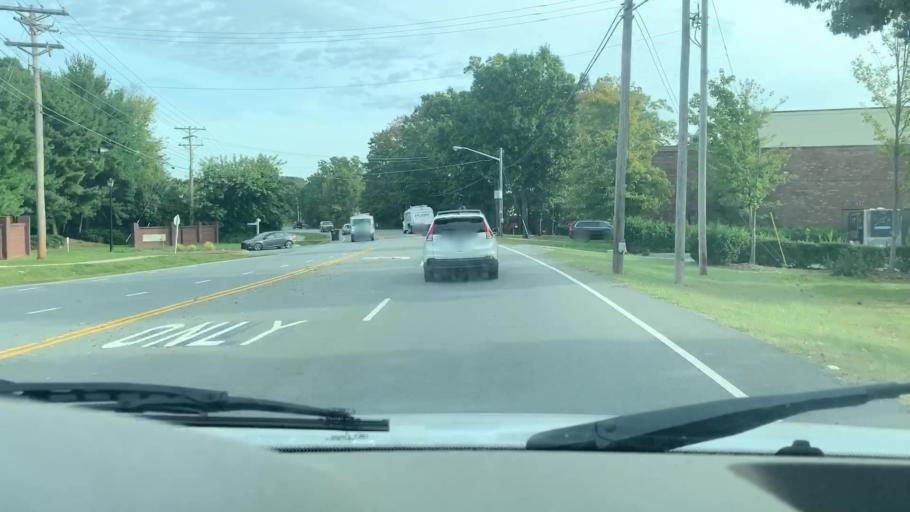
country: US
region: North Carolina
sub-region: Mecklenburg County
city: Cornelius
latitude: 35.4455
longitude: -80.8938
